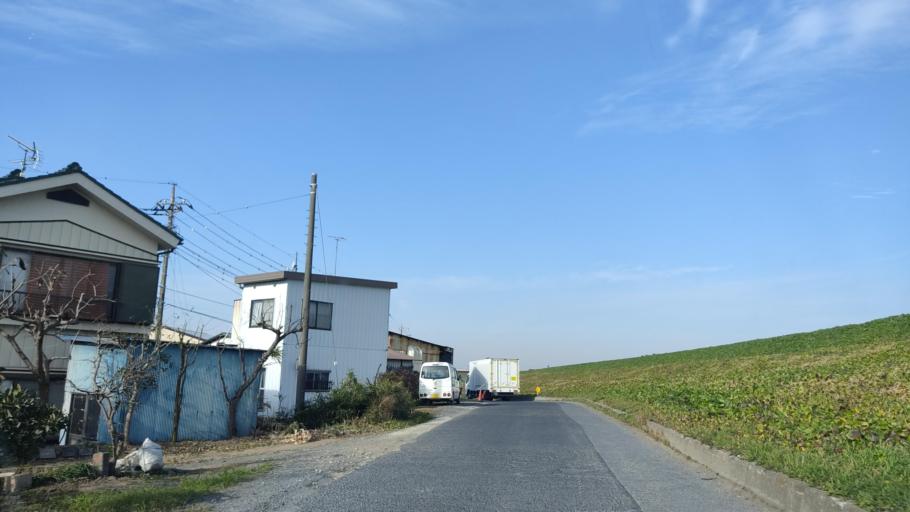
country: JP
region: Chiba
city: Nagareyama
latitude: 35.8669
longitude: 139.8950
